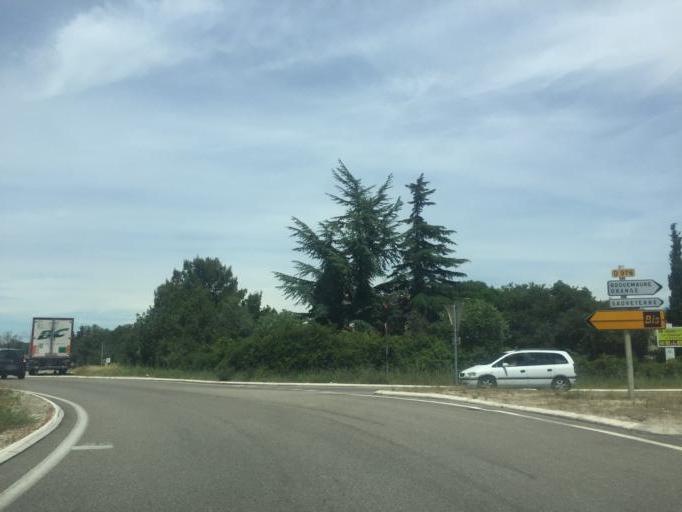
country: FR
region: Languedoc-Roussillon
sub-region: Departement du Gard
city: Pujaut
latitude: 44.0207
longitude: 4.7410
